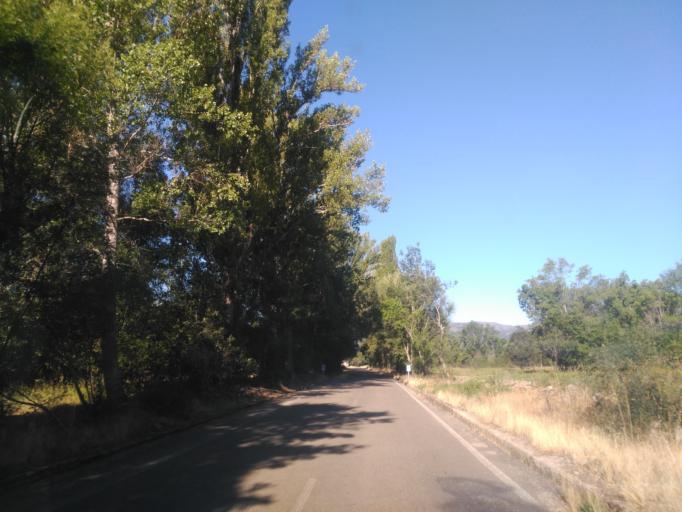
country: ES
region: Castille and Leon
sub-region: Provincia de Zamora
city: Galende
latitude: 42.0875
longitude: -6.6777
